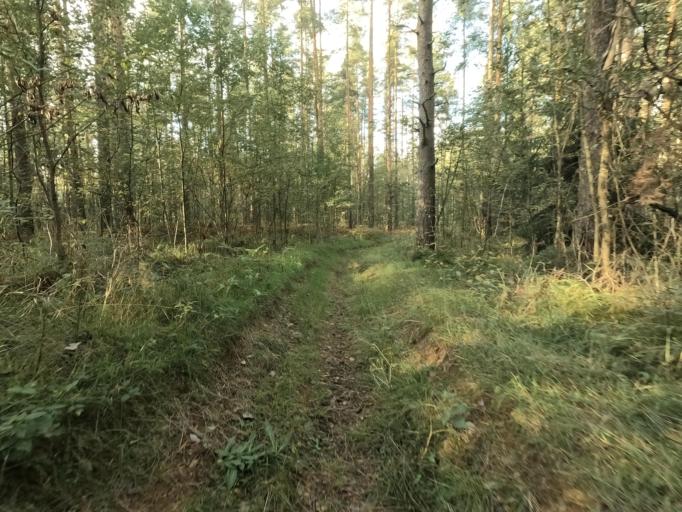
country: RU
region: Leningrad
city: Imeni Sverdlova
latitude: 59.8487
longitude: 30.7280
